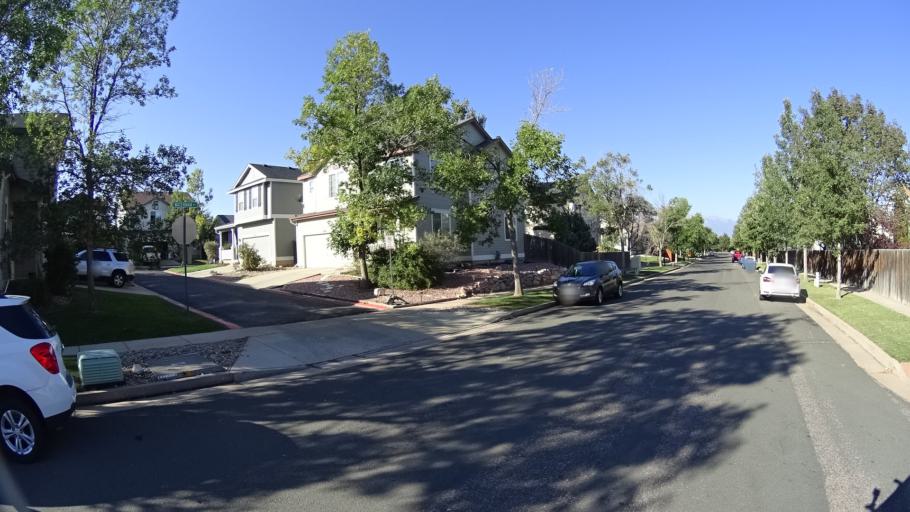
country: US
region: Colorado
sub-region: El Paso County
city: Cimarron Hills
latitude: 38.8760
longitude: -104.6987
